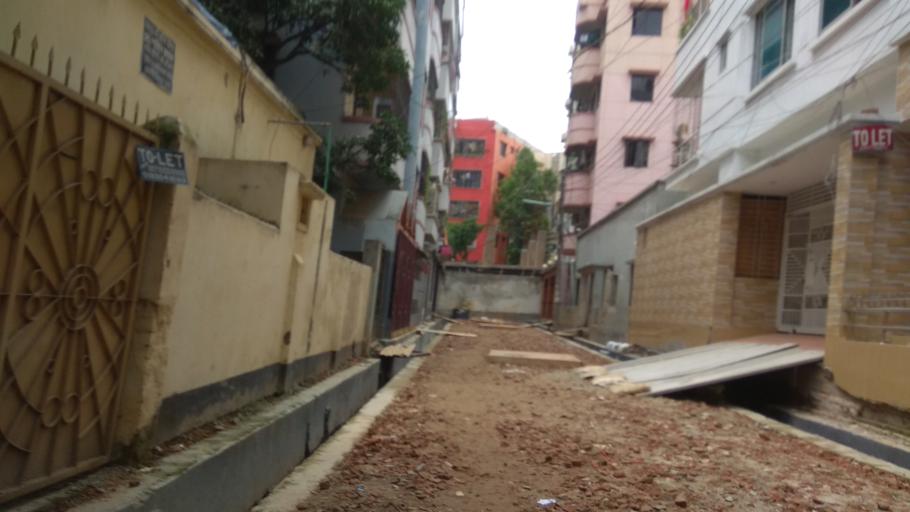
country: BD
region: Dhaka
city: Tungi
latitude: 23.8204
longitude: 90.3577
